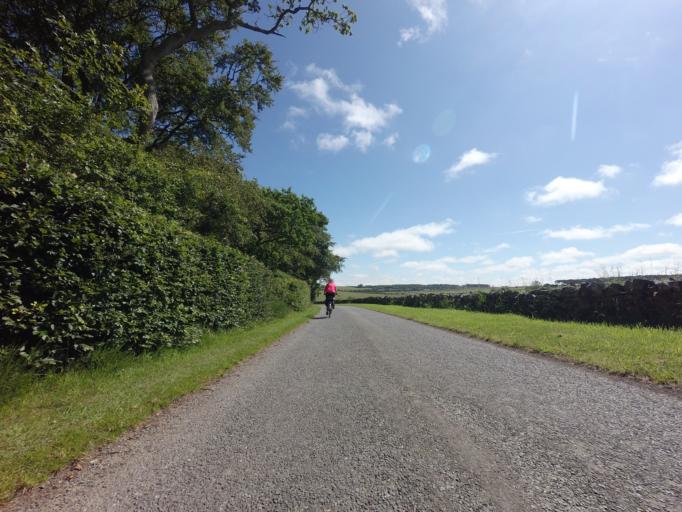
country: GB
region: Scotland
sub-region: Aberdeenshire
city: Macduff
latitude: 57.6212
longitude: -2.5013
